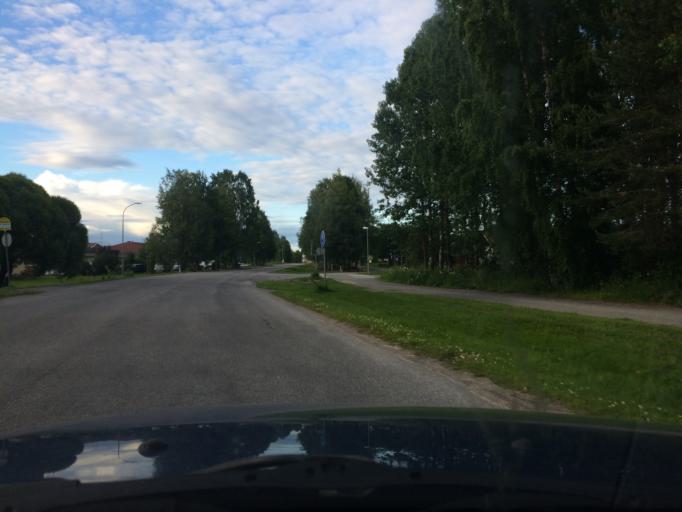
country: SE
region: Norrbotten
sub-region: Pitea Kommun
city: Bergsviken
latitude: 65.3458
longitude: 21.4095
